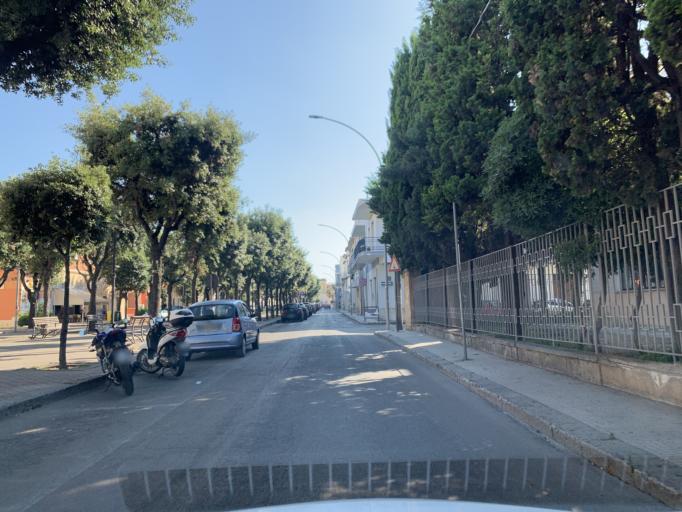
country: IT
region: Apulia
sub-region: Provincia di Lecce
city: Nardo
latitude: 40.1816
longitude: 18.0355
